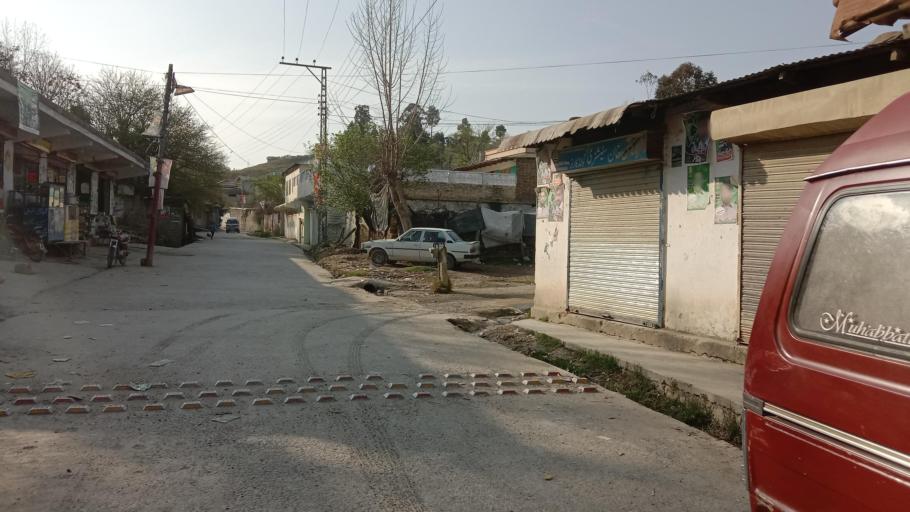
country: PK
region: Khyber Pakhtunkhwa
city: Abbottabad
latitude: 34.2026
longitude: 73.2247
